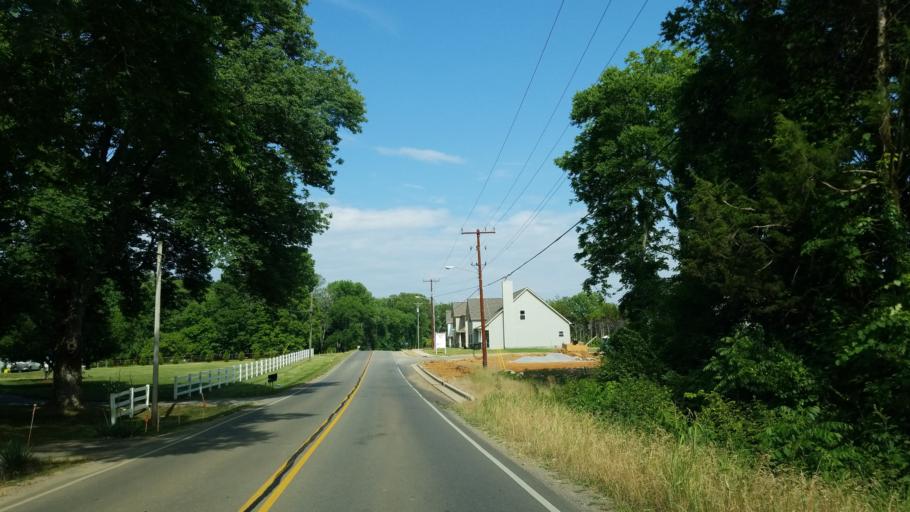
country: US
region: Tennessee
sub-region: Rutherford County
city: La Vergne
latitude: 36.0572
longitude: -86.5935
